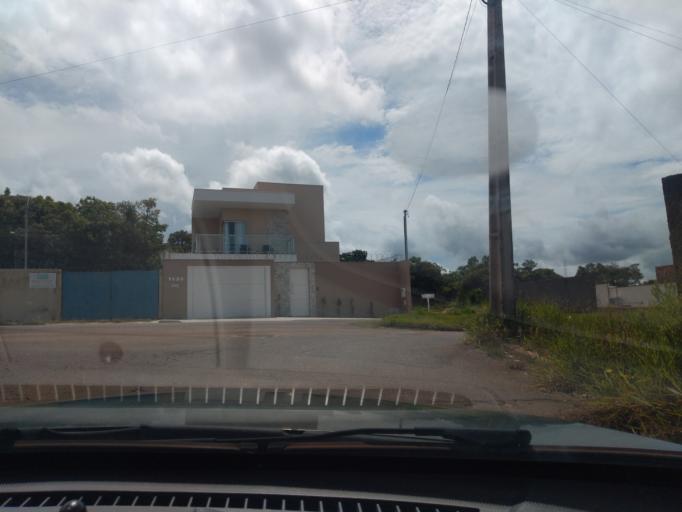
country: BR
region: Minas Gerais
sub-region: Tres Coracoes
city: Tres Coracoes
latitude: -21.6741
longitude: -45.2780
